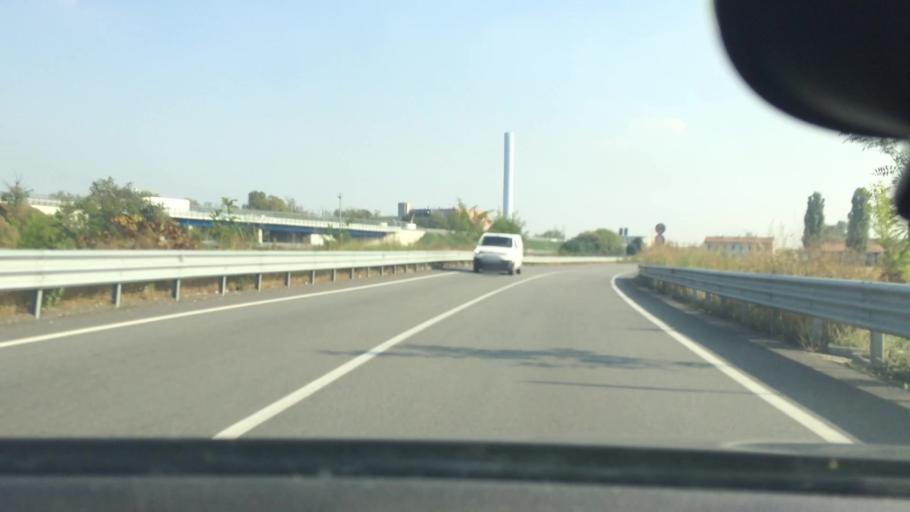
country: IT
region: Lombardy
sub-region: Citta metropolitana di Milano
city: Rho
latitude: 45.5090
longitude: 9.0603
